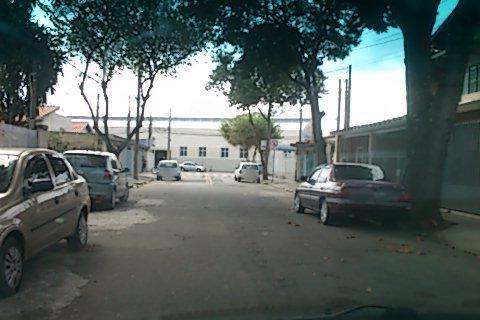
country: BR
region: Sao Paulo
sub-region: Sao Jose Dos Campos
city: Sao Jose dos Campos
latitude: -23.1906
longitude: -45.8724
